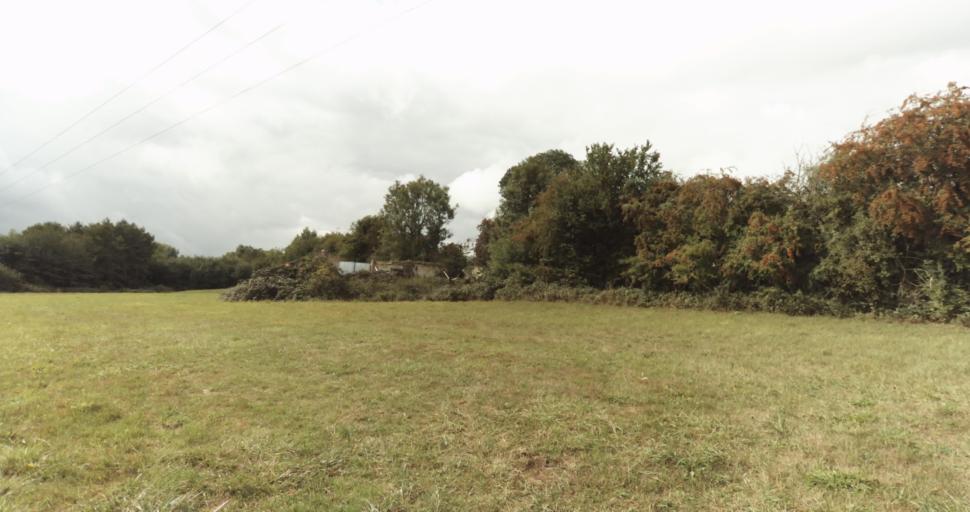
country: FR
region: Lower Normandy
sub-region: Departement de l'Orne
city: Sainte-Gauburge-Sainte-Colombe
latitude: 48.7161
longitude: 0.4153
